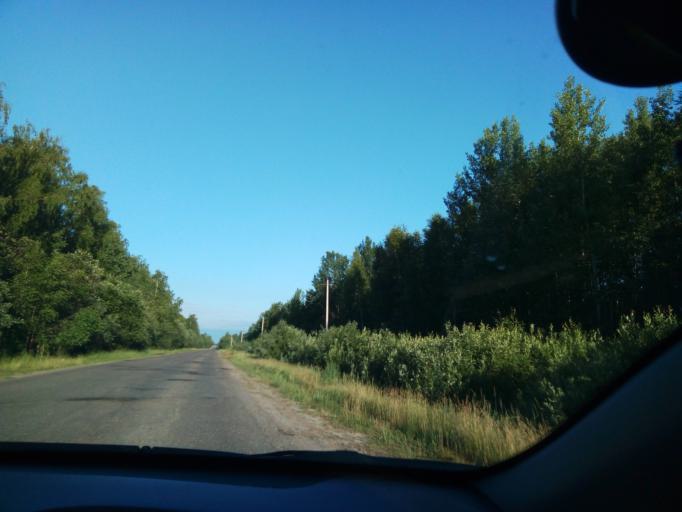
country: RU
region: Nizjnij Novgorod
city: Voznesenskoye
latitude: 54.8907
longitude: 42.8015
